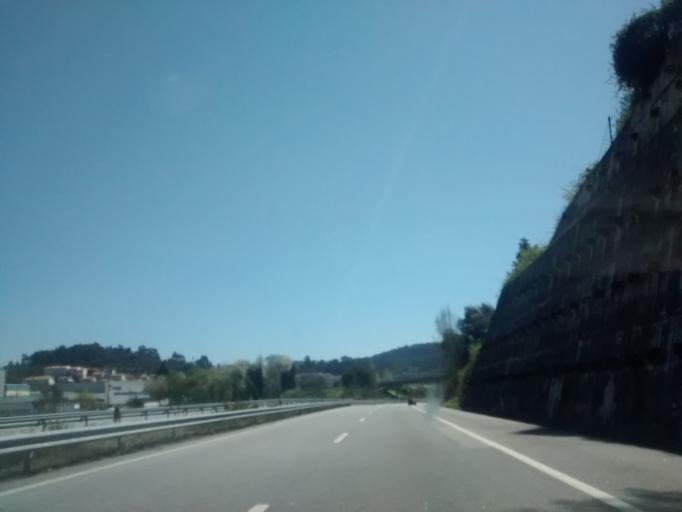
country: PT
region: Braga
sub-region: Guimaraes
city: Candoso
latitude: 41.4195
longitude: -8.3272
